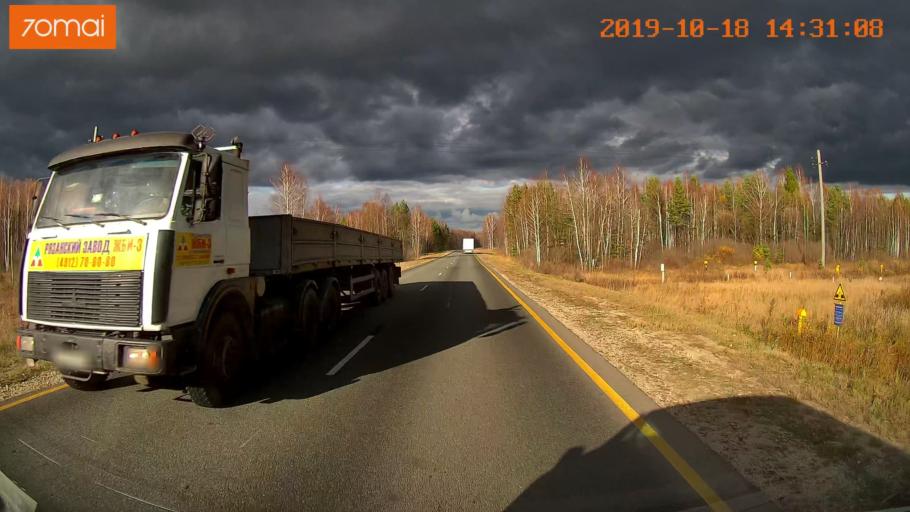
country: RU
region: Rjazan
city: Tuma
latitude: 55.1787
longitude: 40.5687
